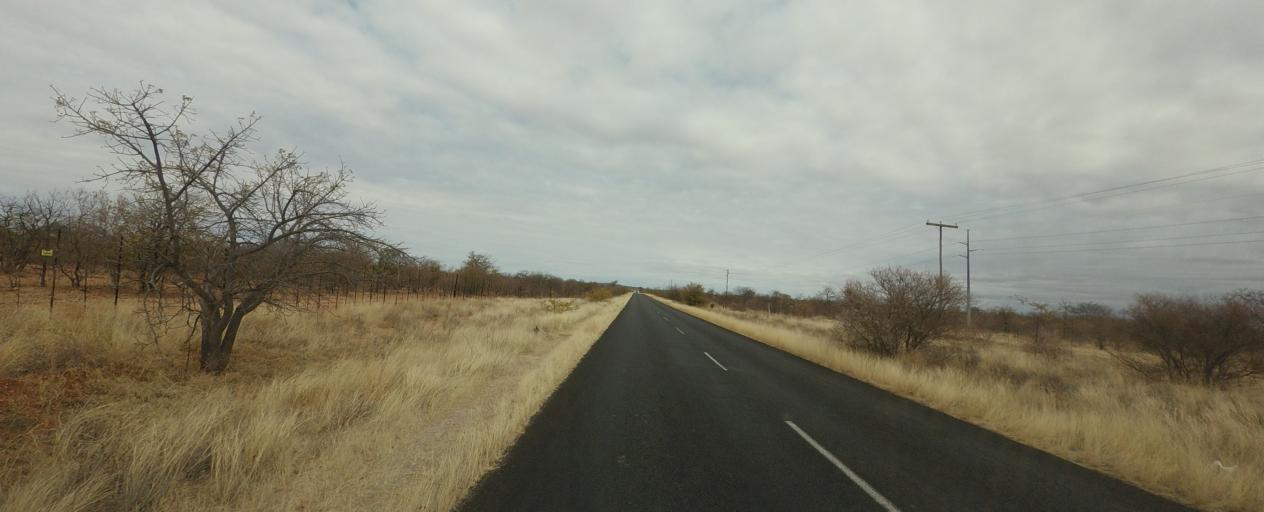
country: ZW
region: Matabeleland South
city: Beitbridge
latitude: -22.4314
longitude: 29.4637
